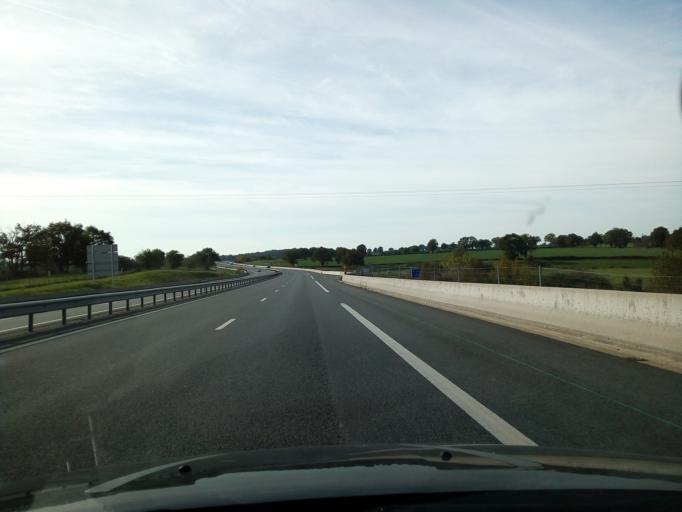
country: FR
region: Auvergne
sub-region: Departement de l'Allier
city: Desertines
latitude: 46.3806
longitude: 2.6848
